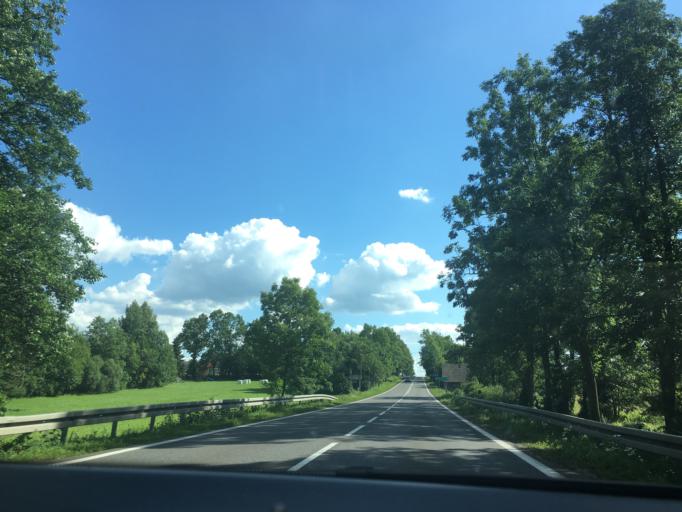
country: PL
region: Podlasie
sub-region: Powiat sokolski
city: Janow
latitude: 53.3950
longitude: 23.1144
